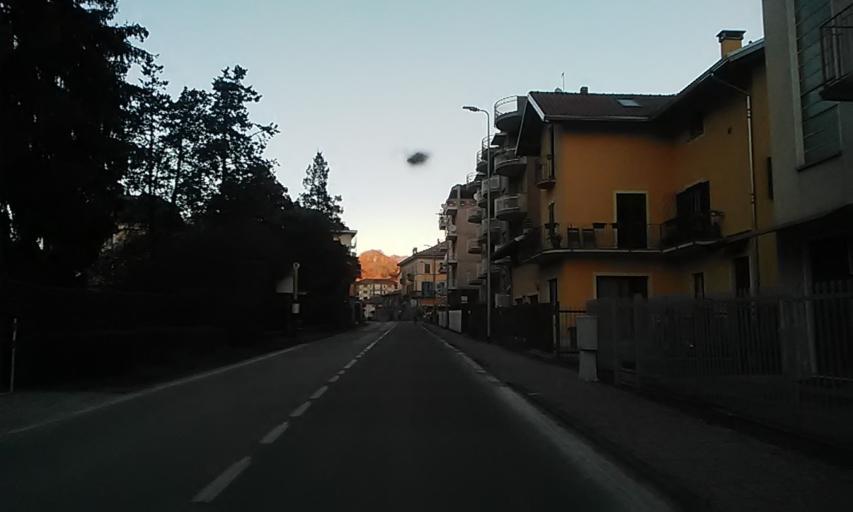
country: IT
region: Piedmont
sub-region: Provincia di Vercelli
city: Quarona
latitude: 45.7587
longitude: 8.2681
